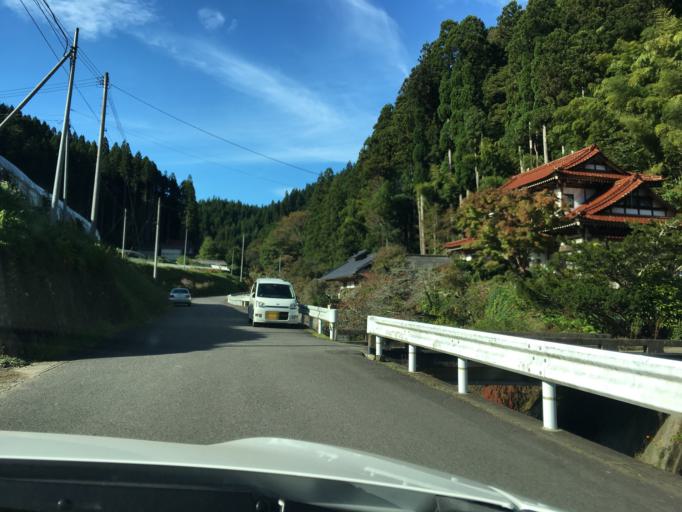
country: JP
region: Fukushima
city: Ishikawa
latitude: 37.1173
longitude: 140.5620
